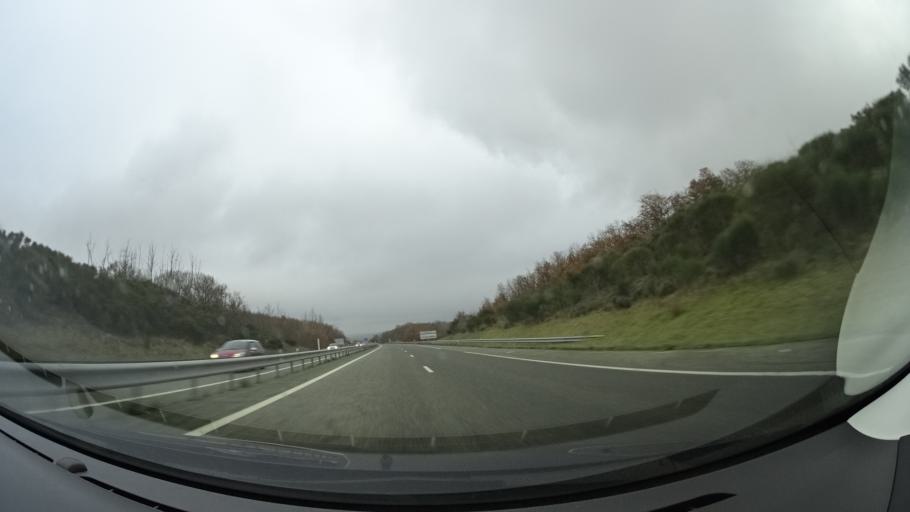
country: FR
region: Midi-Pyrenees
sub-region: Departement de la Haute-Garonne
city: Nailloux
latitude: 43.3925
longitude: 1.6336
